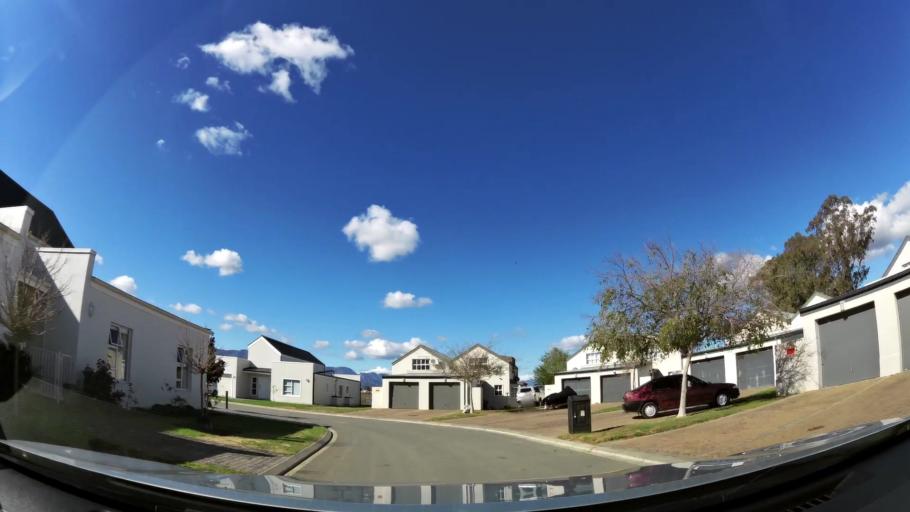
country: ZA
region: Western Cape
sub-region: Cape Winelands District Municipality
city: Ashton
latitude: -33.8121
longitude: 19.8571
